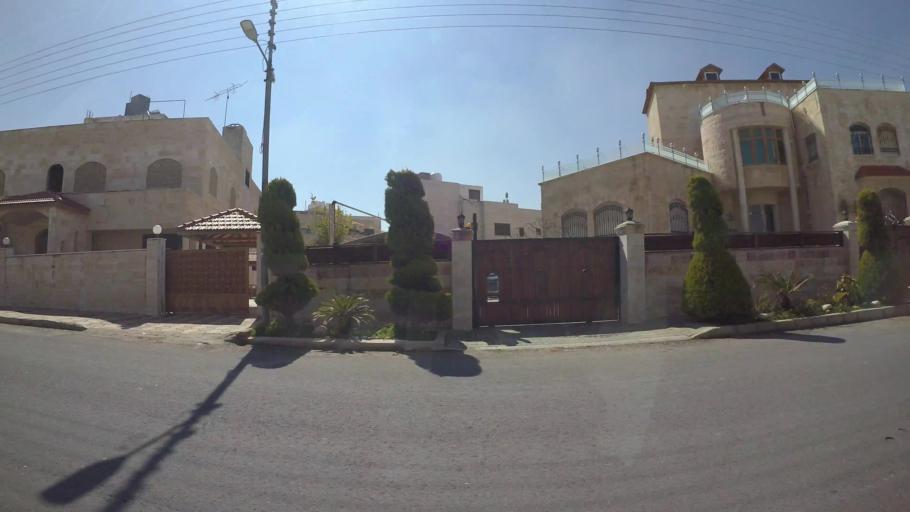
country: JO
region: Amman
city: Al Bunayyat ash Shamaliyah
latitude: 31.8985
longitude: 35.8824
